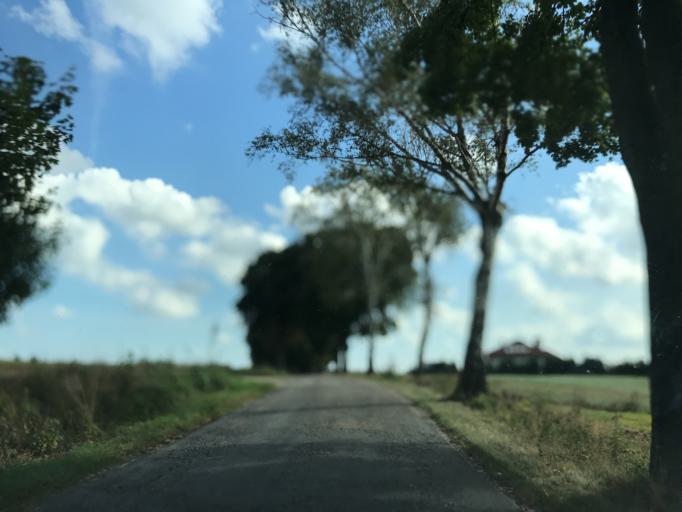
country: PL
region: Kujawsko-Pomorskie
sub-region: Powiat brodnicki
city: Brzozie
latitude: 53.3542
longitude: 19.6907
